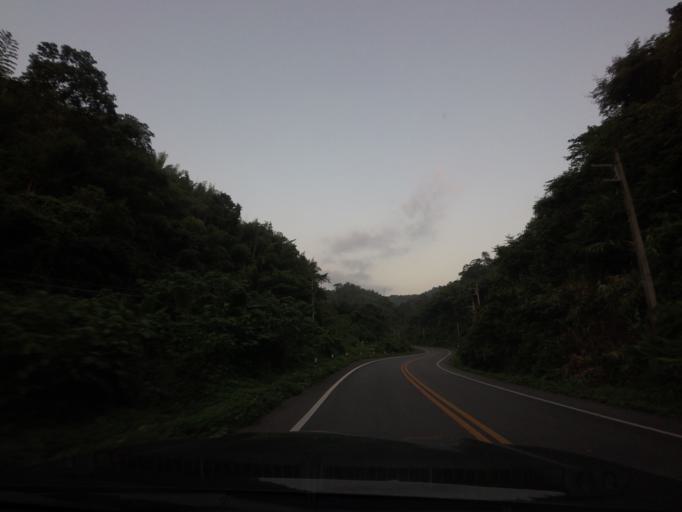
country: TH
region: Nan
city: Na Noi
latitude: 18.4304
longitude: 100.7004
